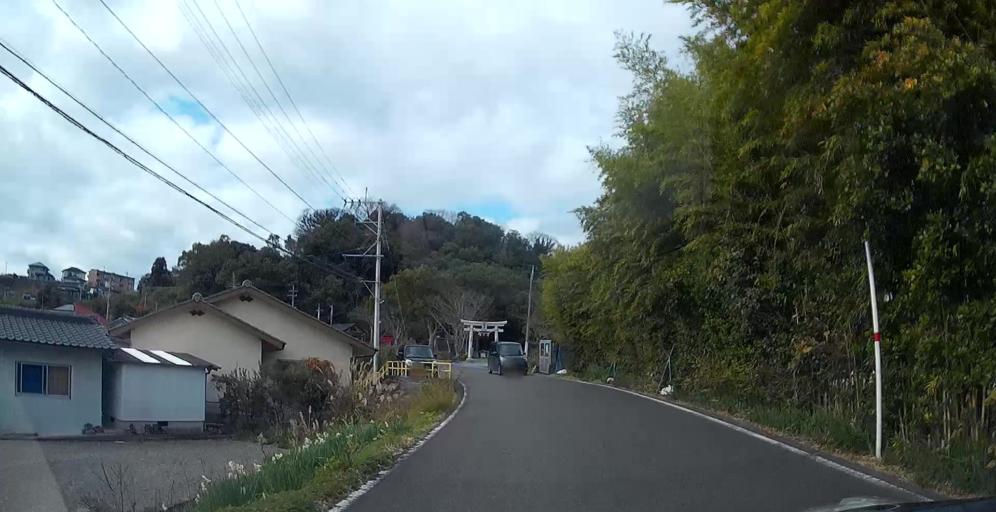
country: JP
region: Kumamoto
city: Minamata
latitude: 32.2122
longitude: 130.3866
